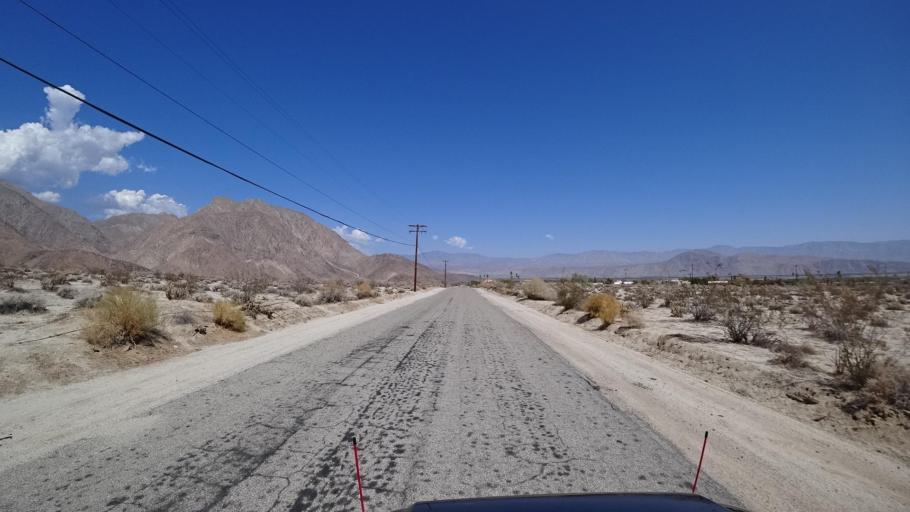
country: US
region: California
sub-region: San Diego County
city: Borrego Springs
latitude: 33.2576
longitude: -116.3995
